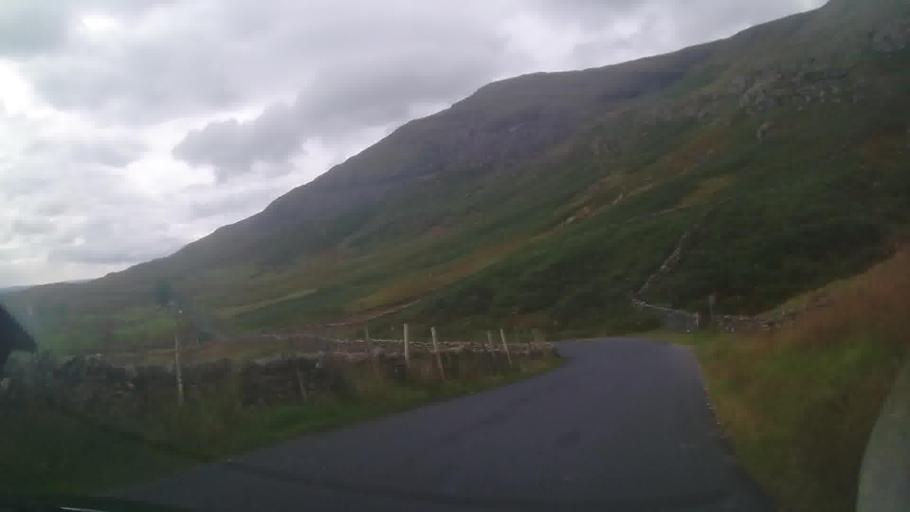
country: GB
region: England
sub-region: Cumbria
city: Ambleside
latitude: 54.4606
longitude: -2.9299
